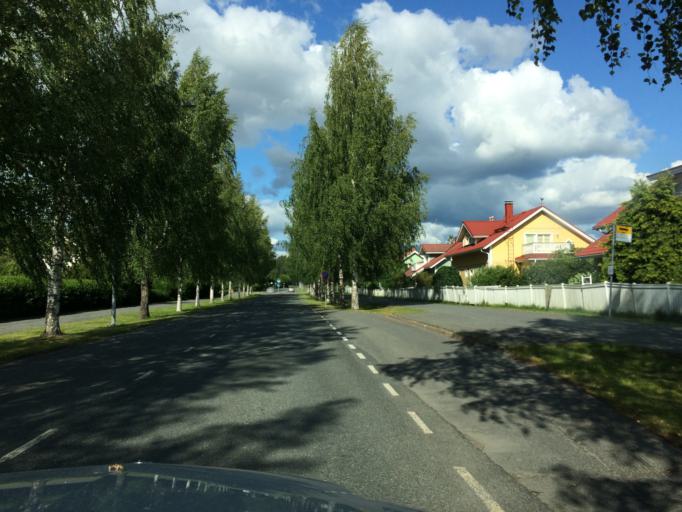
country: FI
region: Haeme
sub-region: Haemeenlinna
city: Parola
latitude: 60.9870
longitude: 24.3918
